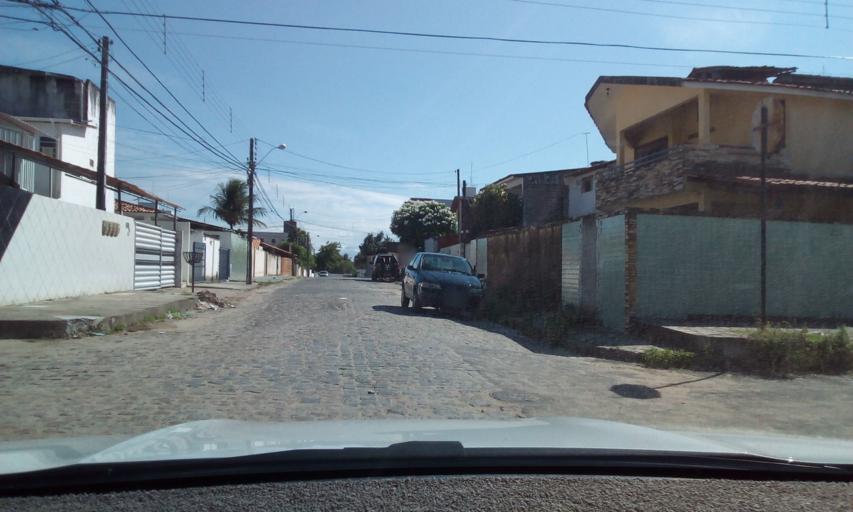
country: BR
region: Paraiba
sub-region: Joao Pessoa
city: Joao Pessoa
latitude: -7.1525
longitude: -34.8480
